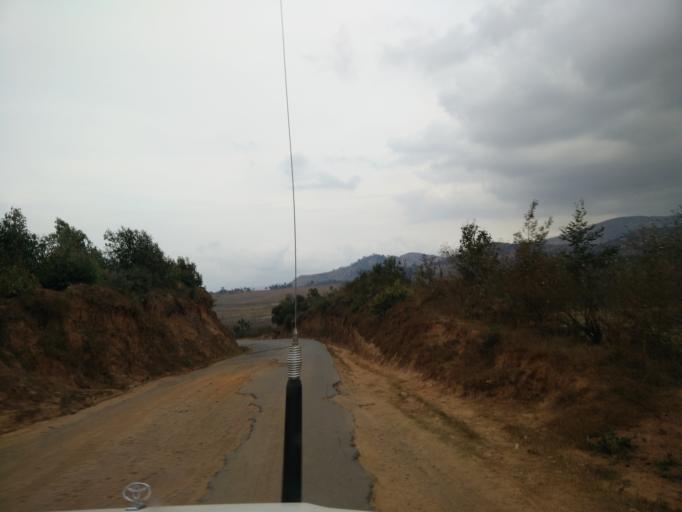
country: MG
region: Upper Matsiatra
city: Fianarantsoa
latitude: -21.5916
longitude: 47.0136
